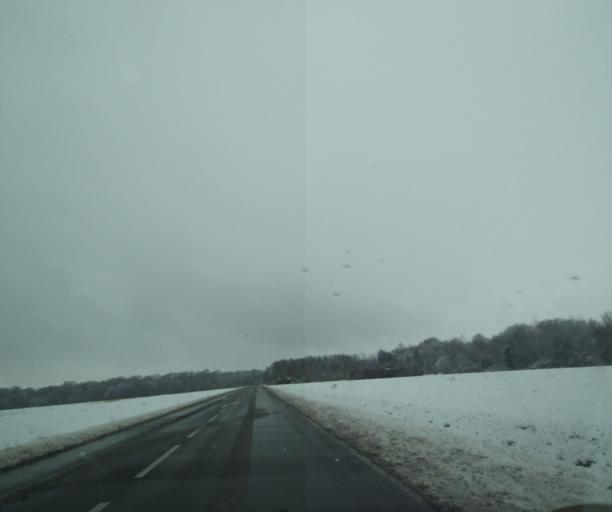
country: FR
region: Champagne-Ardenne
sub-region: Departement de la Haute-Marne
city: Montier-en-Der
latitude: 48.4963
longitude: 4.7829
